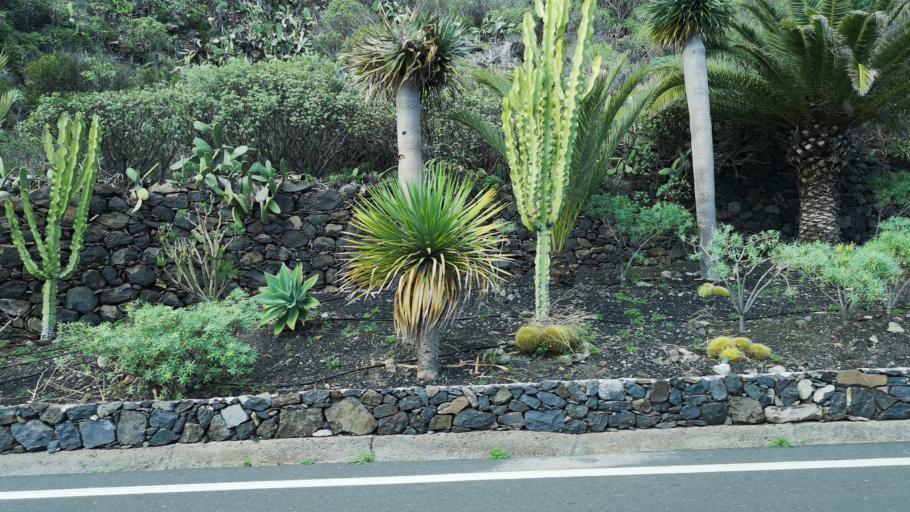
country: ES
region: Canary Islands
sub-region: Provincia de Santa Cruz de Tenerife
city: Agulo
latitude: 28.1801
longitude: -17.1862
